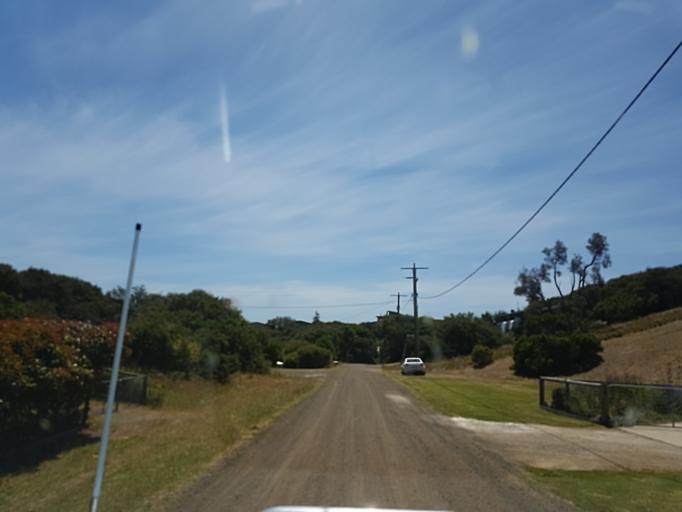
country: AU
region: Victoria
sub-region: Bass Coast
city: North Wonthaggi
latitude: -38.7008
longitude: 145.8267
